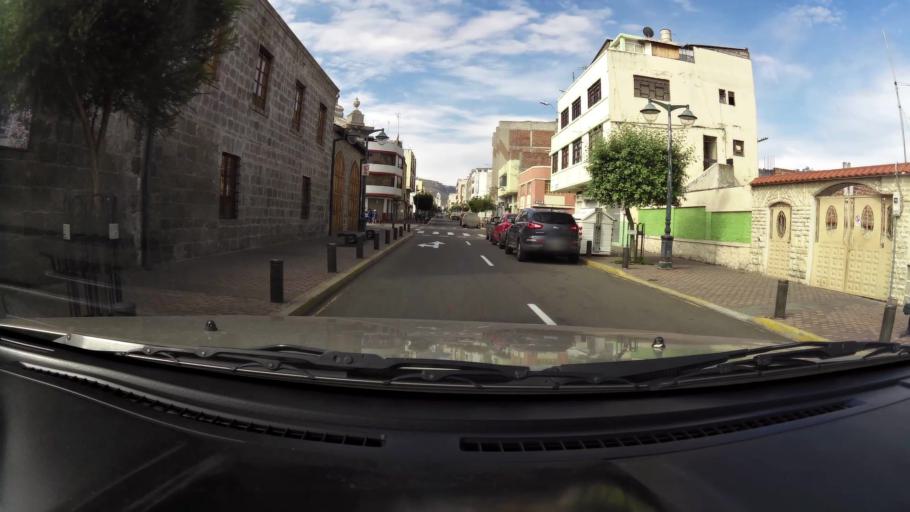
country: EC
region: Tungurahua
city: Ambato
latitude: -1.2410
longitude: -78.6286
